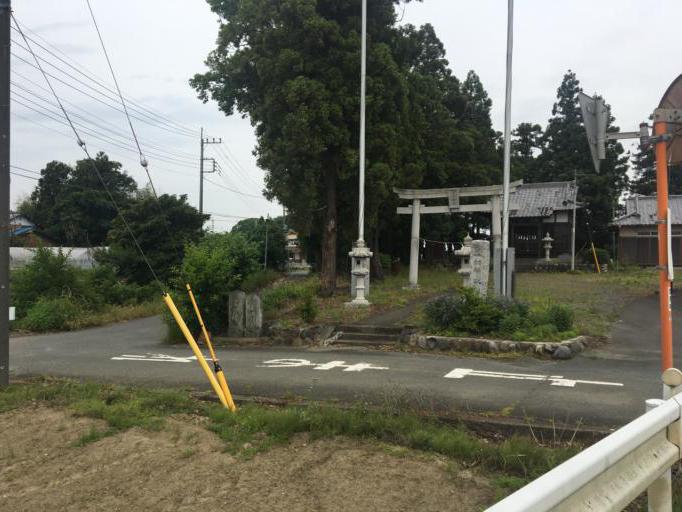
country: JP
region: Saitama
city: Konosu
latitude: 36.0246
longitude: 139.4575
